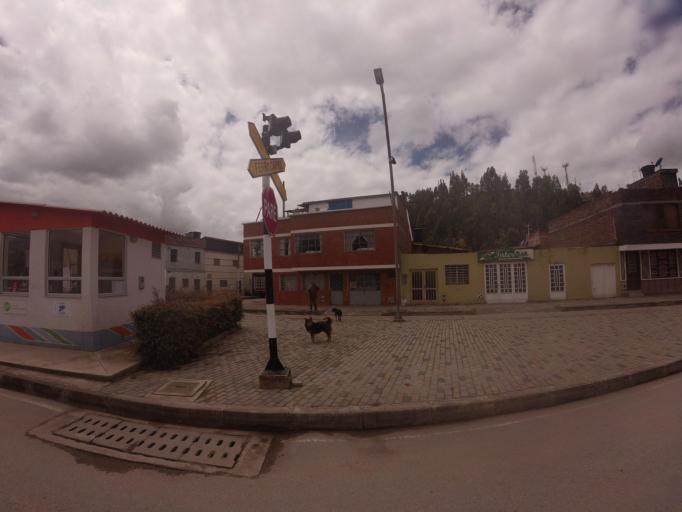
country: CO
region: Boyaca
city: Duitama
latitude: 5.8247
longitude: -73.0308
